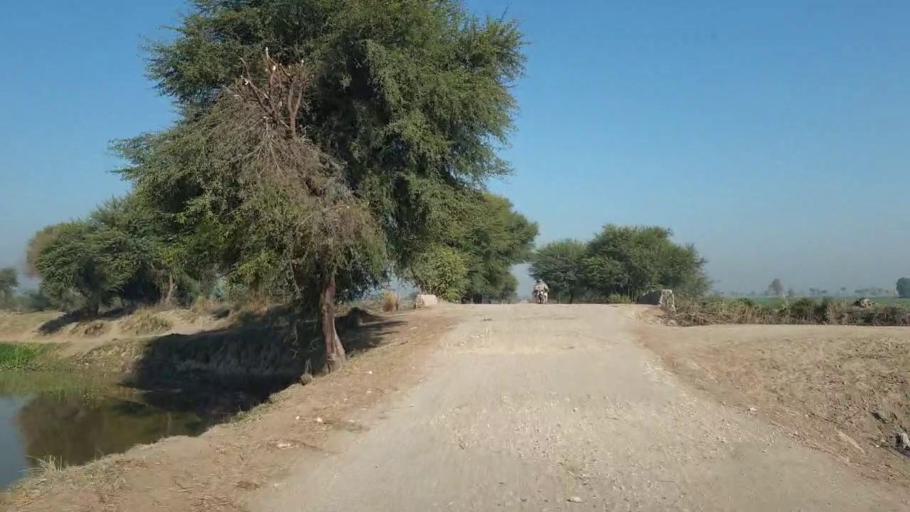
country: PK
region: Sindh
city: Shahdadpur
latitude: 25.9346
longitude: 68.5046
